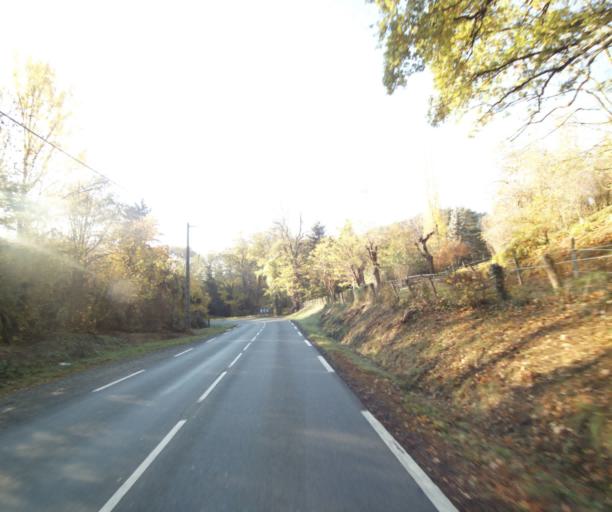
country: FR
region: Auvergne
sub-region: Departement du Puy-de-Dome
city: Nohanent
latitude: 45.8089
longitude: 3.0498
